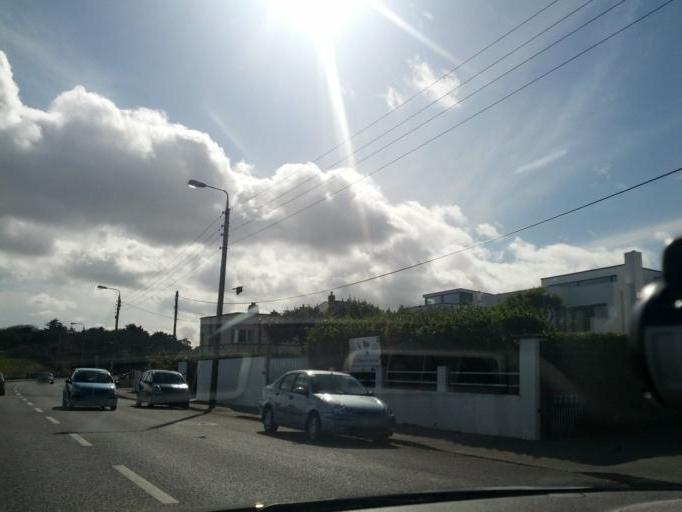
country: IE
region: Leinster
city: Portmarnock
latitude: 53.4331
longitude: -6.1245
